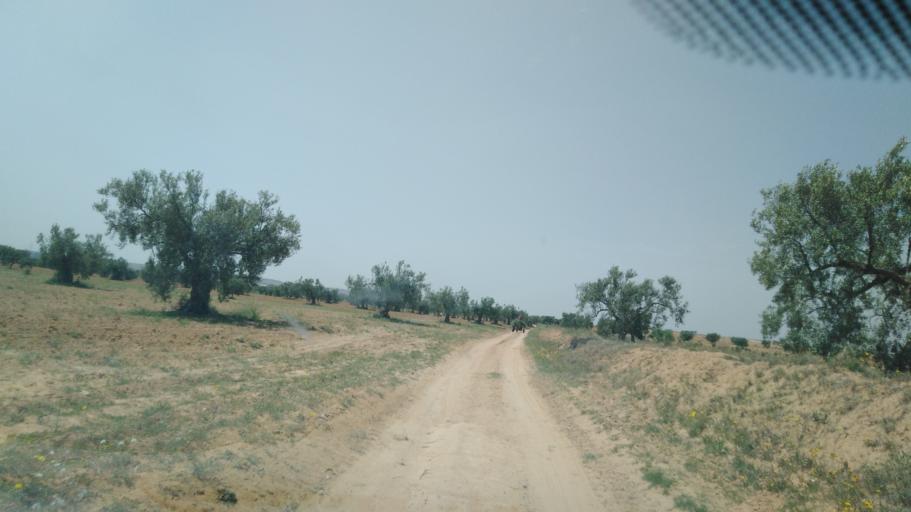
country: TN
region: Safaqis
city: Sfax
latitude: 34.7639
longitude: 10.5800
